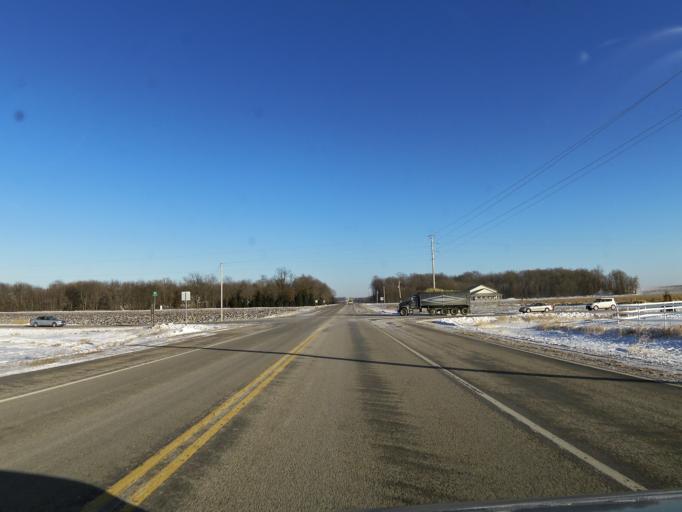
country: US
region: Minnesota
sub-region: Le Sueur County
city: Montgomery
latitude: 44.4863
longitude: -93.5662
